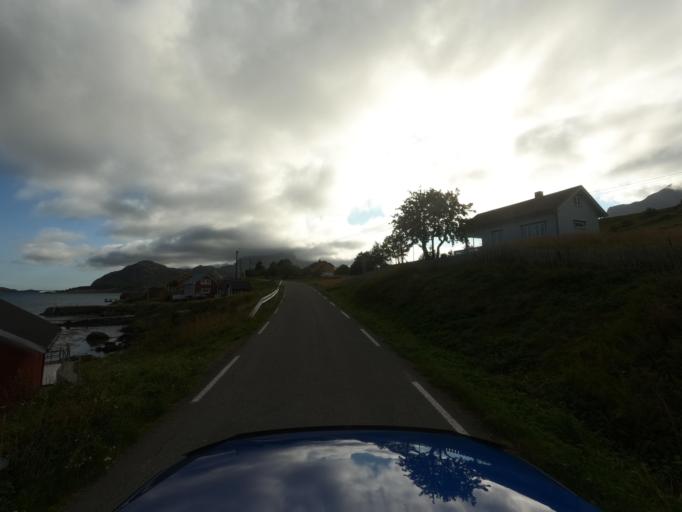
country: NO
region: Nordland
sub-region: Flakstad
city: Ramberg
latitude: 68.0573
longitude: 13.1570
